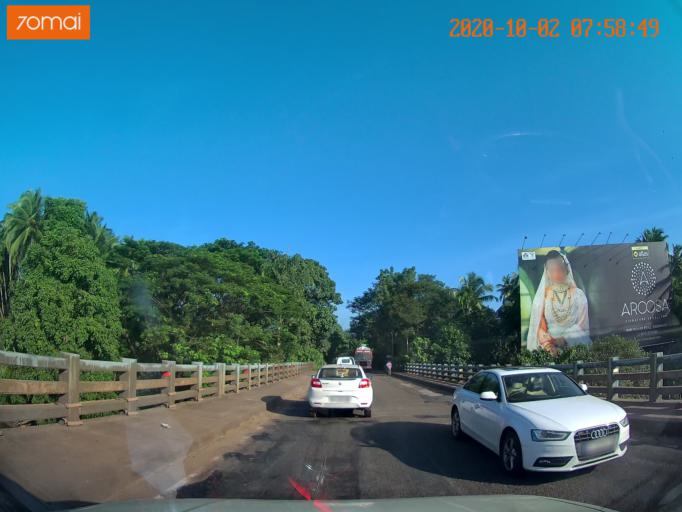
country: IN
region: Kerala
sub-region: Kozhikode
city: Ferokh
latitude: 11.2065
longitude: 75.8640
